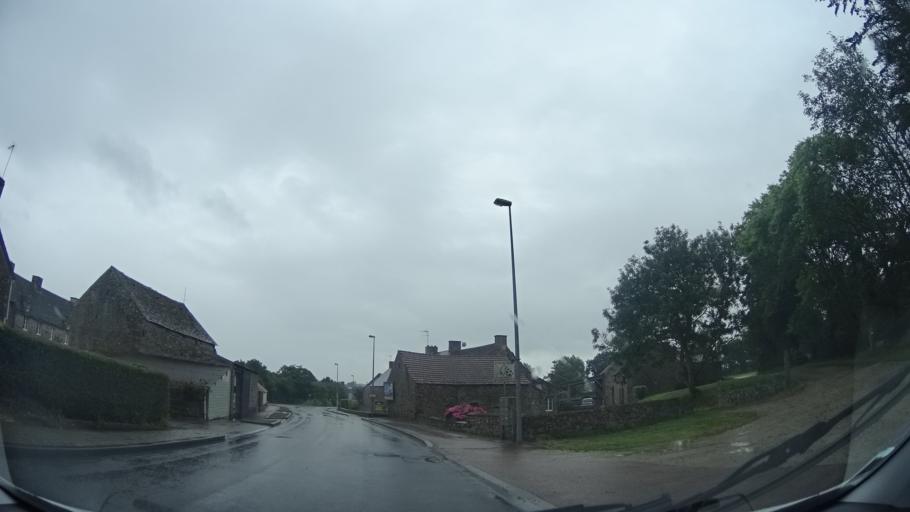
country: FR
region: Lower Normandy
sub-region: Departement de la Manche
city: Beaumont-Hague
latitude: 49.5995
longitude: -1.7804
